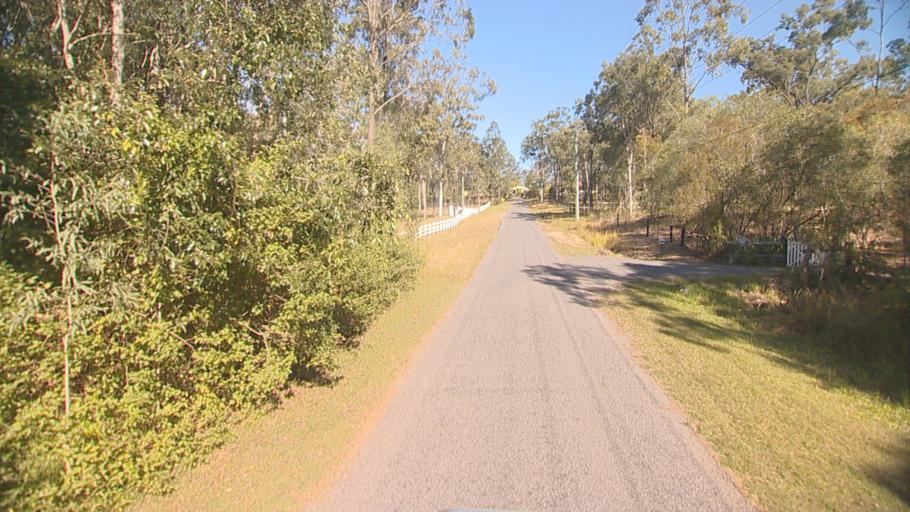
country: AU
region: Queensland
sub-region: Logan
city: Chambers Flat
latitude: -27.8190
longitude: 153.0768
